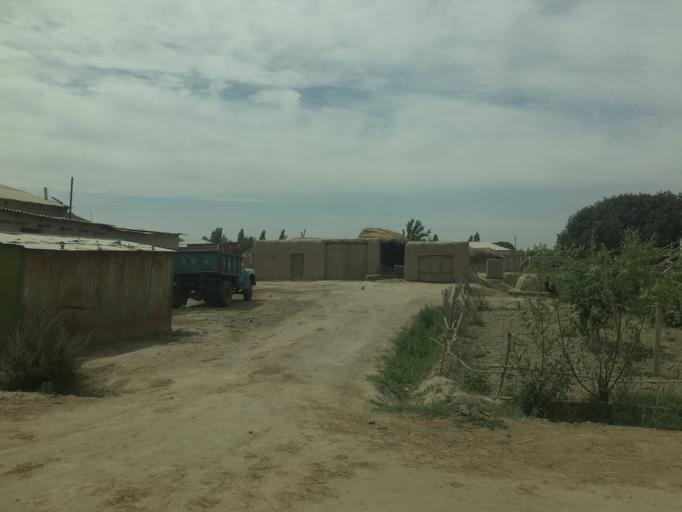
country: TM
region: Dasoguz
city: Tagta
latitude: 41.6114
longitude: 59.8296
